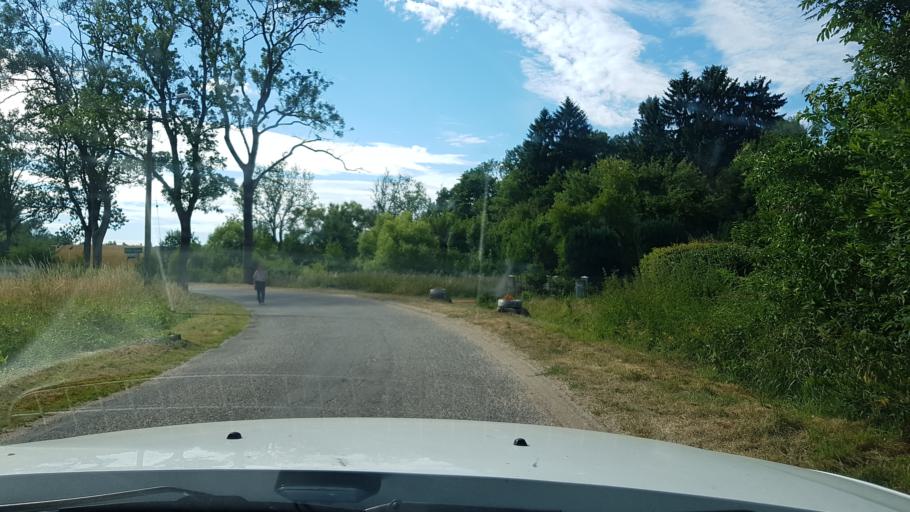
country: PL
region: West Pomeranian Voivodeship
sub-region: Powiat drawski
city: Zlocieniec
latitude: 53.6301
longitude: 16.0749
